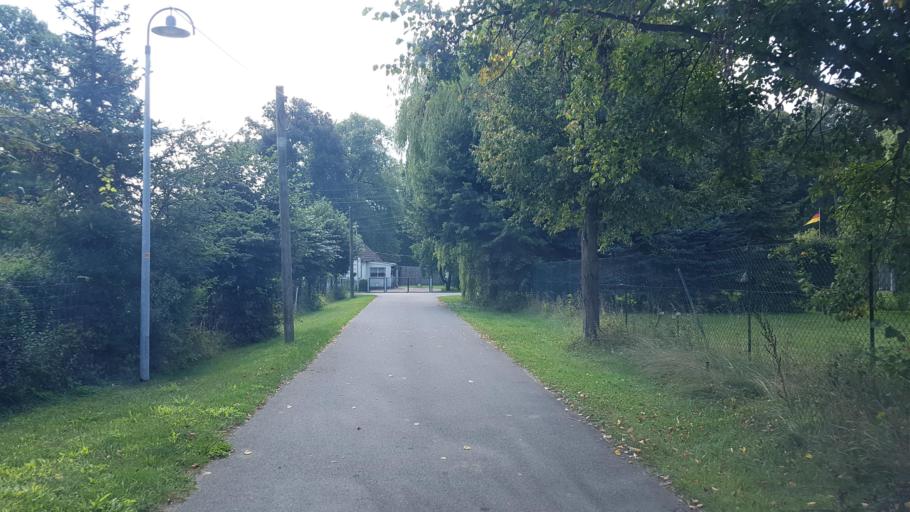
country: DE
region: Brandenburg
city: Drahnsdorf
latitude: 51.8166
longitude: 13.6031
